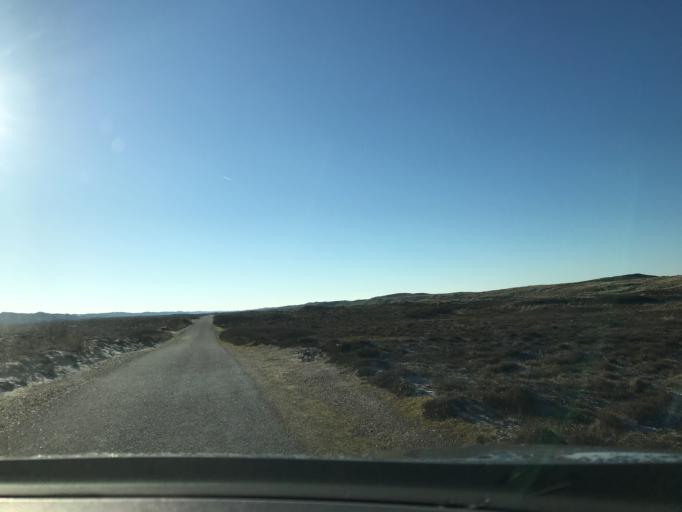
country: DK
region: South Denmark
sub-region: Varde Kommune
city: Oksbol
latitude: 55.7990
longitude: 8.1820
